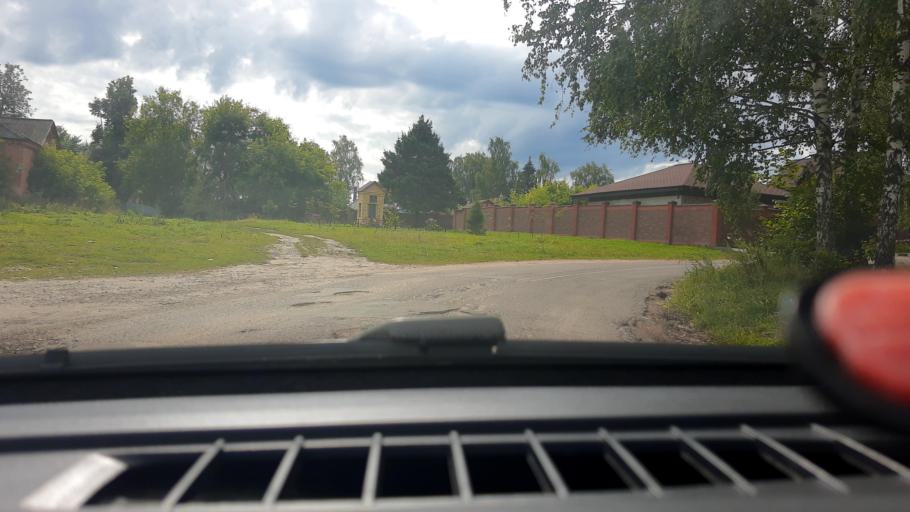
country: RU
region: Nizjnij Novgorod
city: Burevestnik
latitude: 56.0343
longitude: 43.7199
